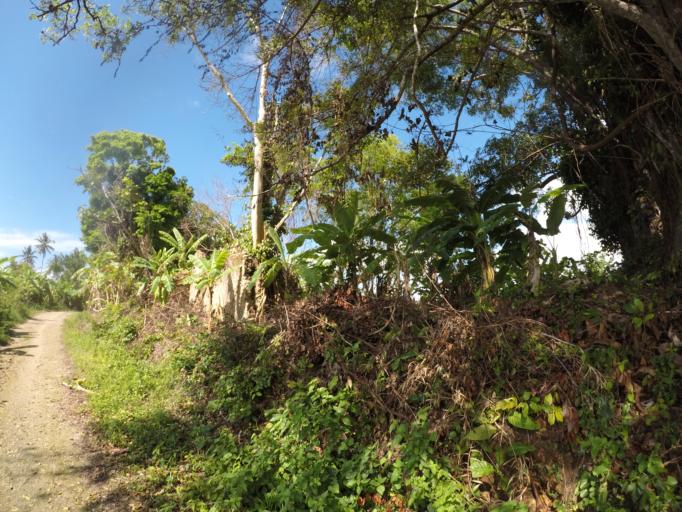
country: TZ
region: Pemba South
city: Mtambile
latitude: -5.3476
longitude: 39.6904
